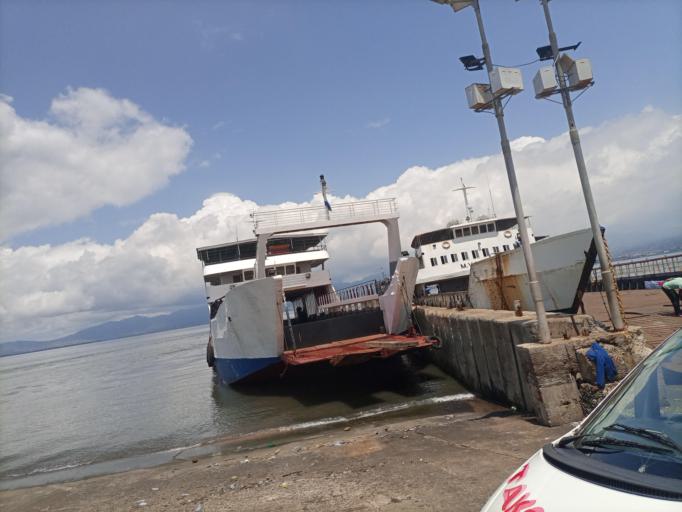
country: SL
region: Western Area
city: Freetown
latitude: 8.5168
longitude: -13.1474
